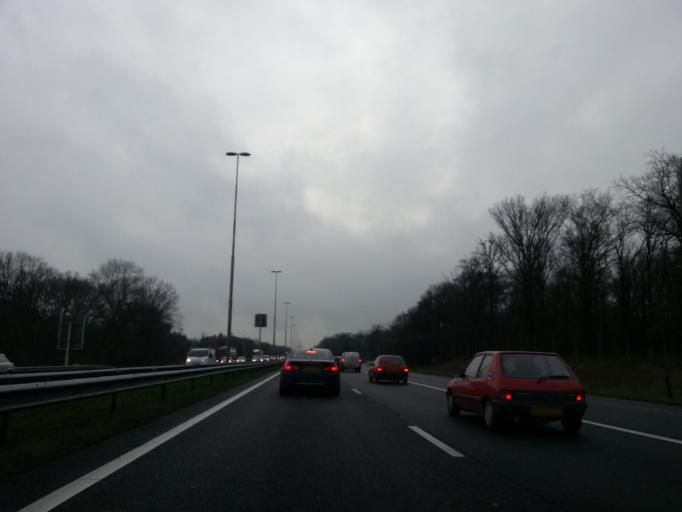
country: NL
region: Gelderland
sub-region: Gemeente Apeldoorn
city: Beekbergen
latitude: 52.0853
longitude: 5.9481
